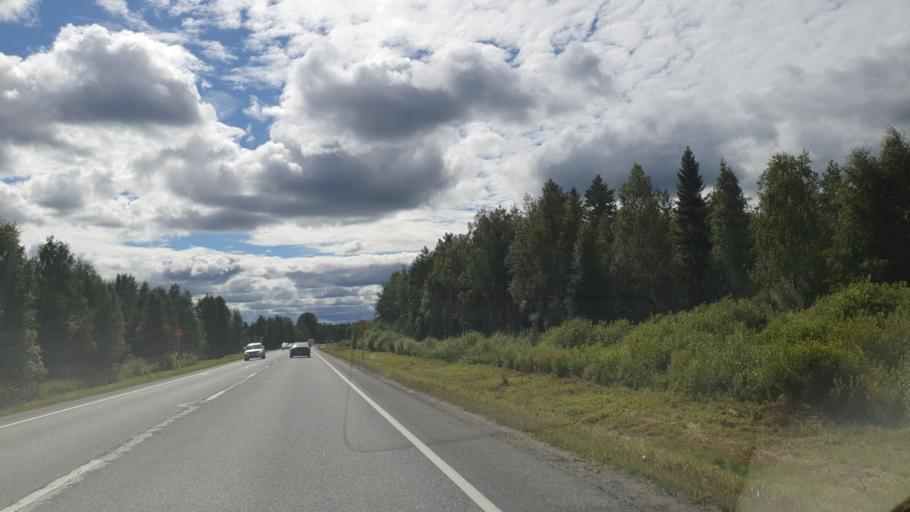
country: FI
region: Kainuu
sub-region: Kajaani
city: Kajaani
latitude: 64.1253
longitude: 27.4685
